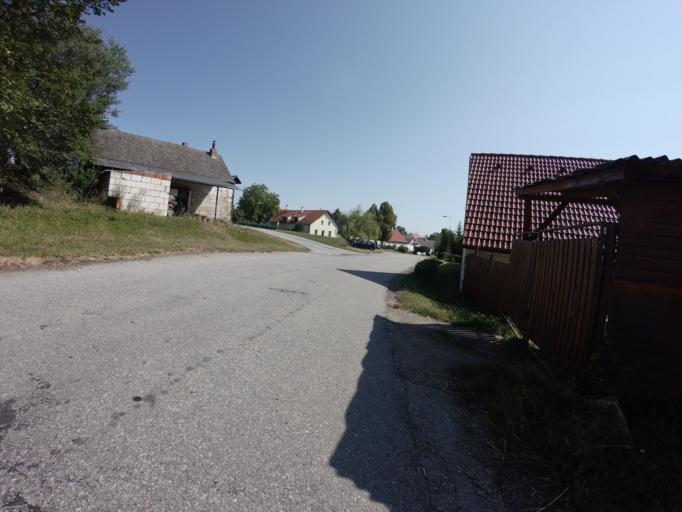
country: CZ
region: Jihocesky
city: Kamenny Ujezd
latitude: 48.8749
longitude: 14.3793
